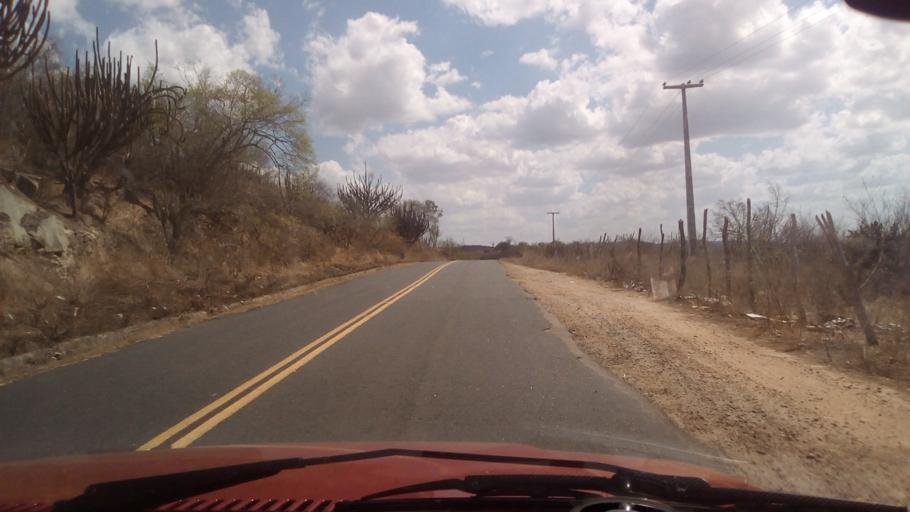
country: BR
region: Paraiba
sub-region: Cacimba De Dentro
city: Cacimba de Dentro
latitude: -6.6804
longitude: -35.7427
